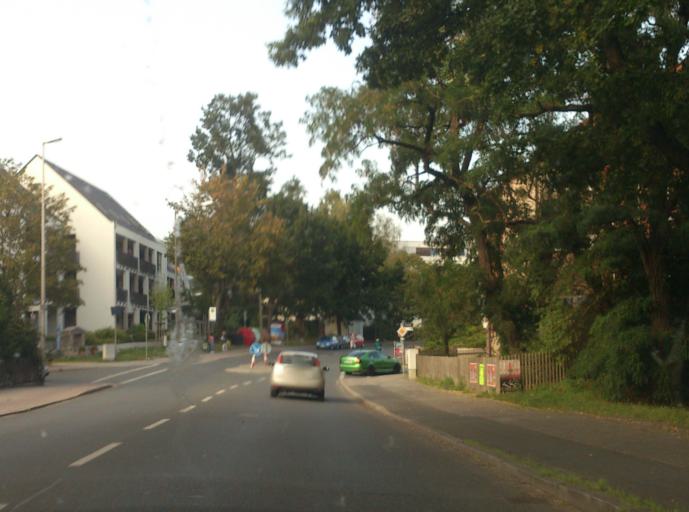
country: DE
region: Bavaria
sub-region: Regierungsbezirk Mittelfranken
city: Buckenhof
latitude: 49.5988
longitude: 11.0374
